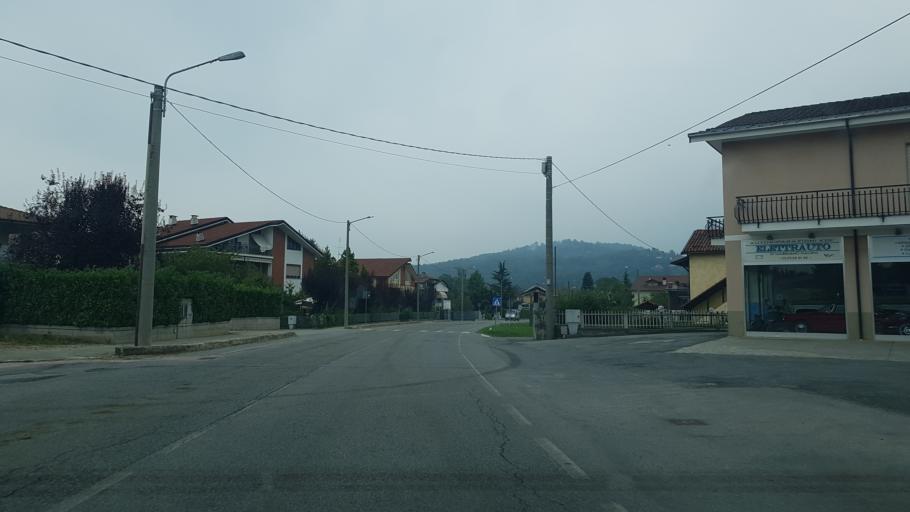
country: IT
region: Piedmont
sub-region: Provincia di Cuneo
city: Villanova Mondovi
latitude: 44.3470
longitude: 7.7734
